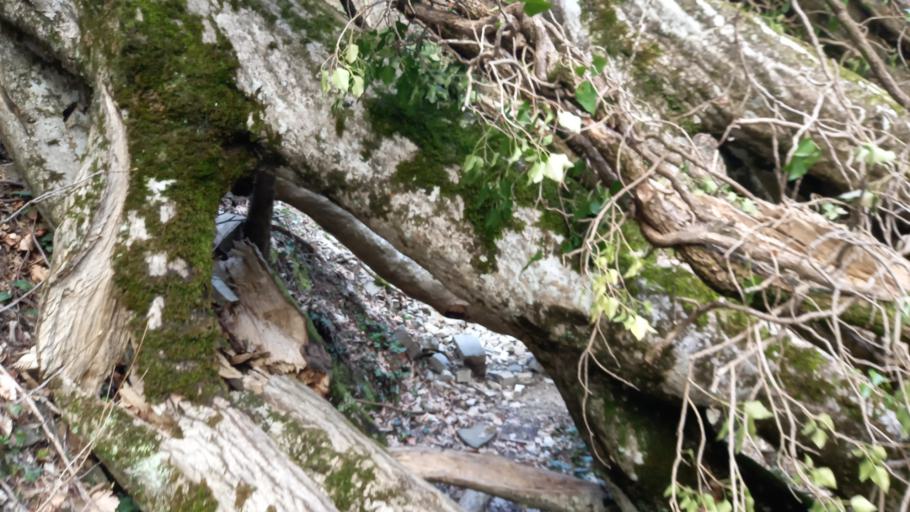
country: RU
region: Krasnodarskiy
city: Pshada
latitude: 44.5134
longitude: 38.4036
